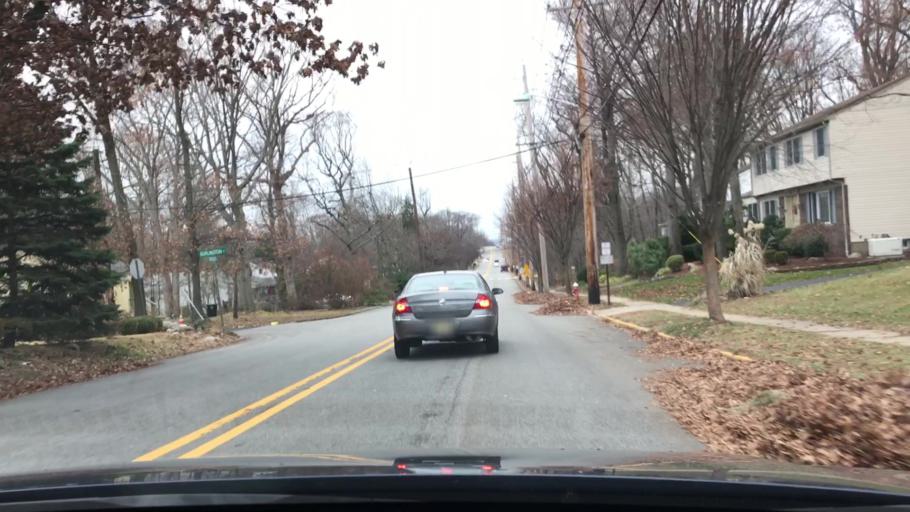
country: US
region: New Jersey
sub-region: Bergen County
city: Oradell
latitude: 40.9531
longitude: -74.0442
